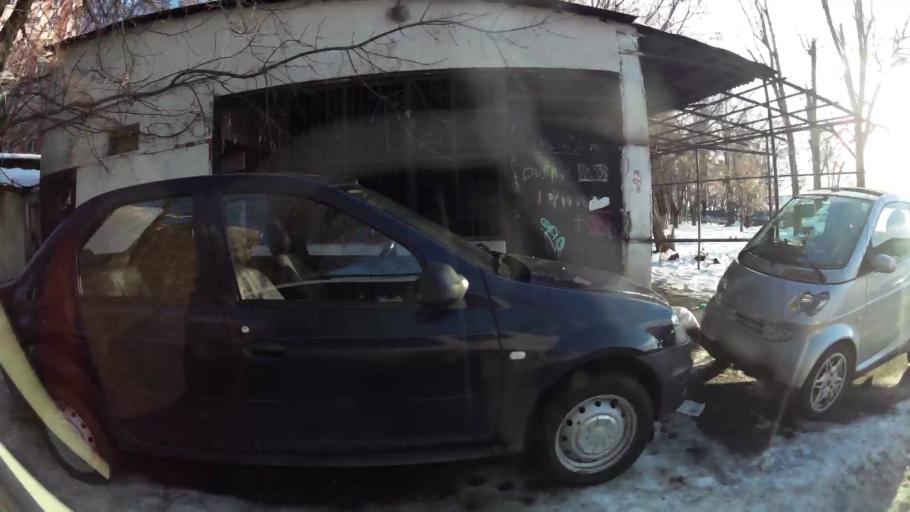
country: RO
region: Bucuresti
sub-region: Municipiul Bucuresti
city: Bucuresti
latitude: 44.3855
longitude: 26.0880
